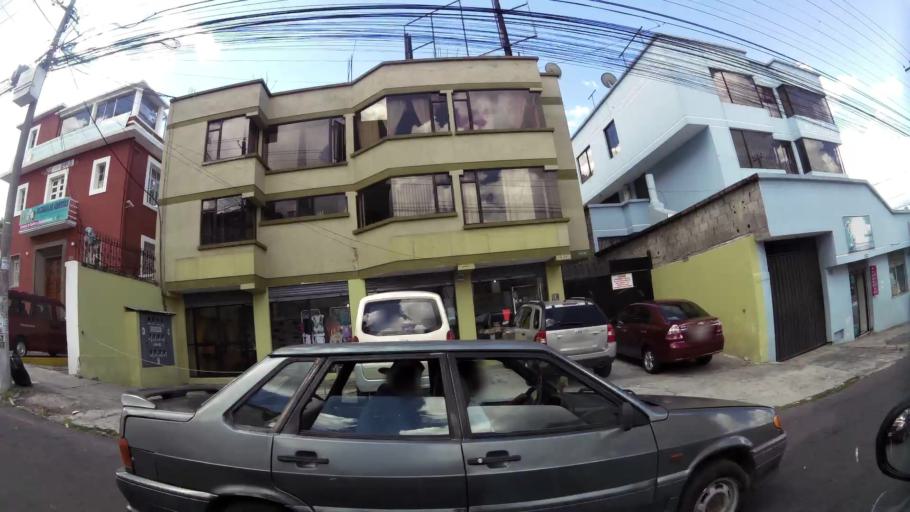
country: EC
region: Pichincha
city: Quito
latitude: -0.1922
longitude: -78.4970
